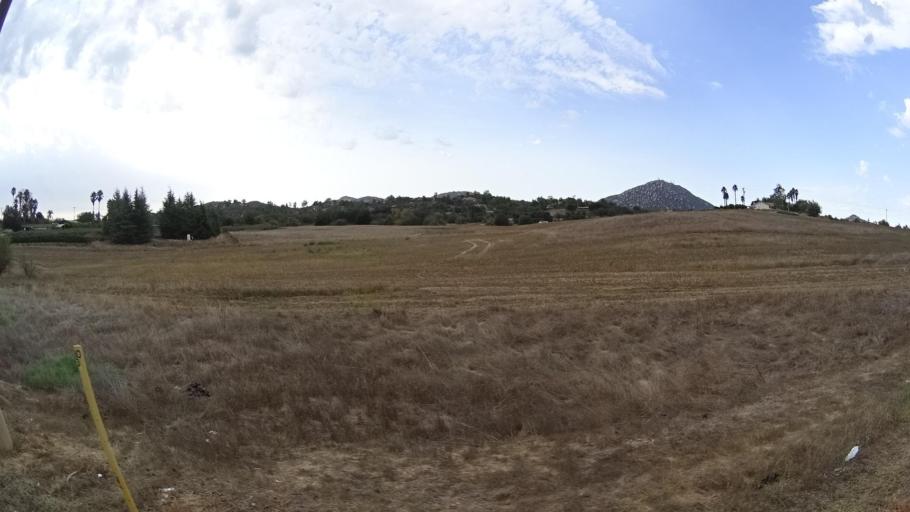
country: US
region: California
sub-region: San Diego County
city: Ramona
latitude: 33.0264
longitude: -116.9338
